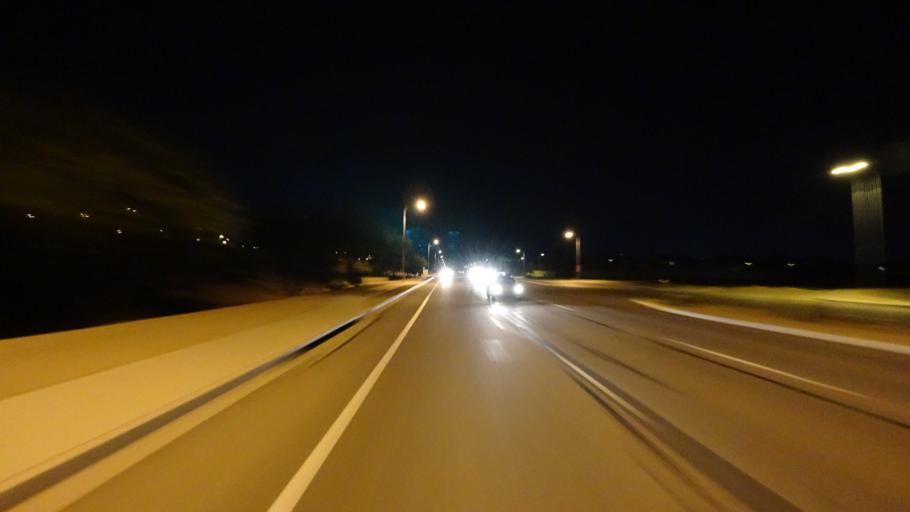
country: US
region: Arizona
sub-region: Maricopa County
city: Chandler
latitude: 33.2493
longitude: -111.8241
